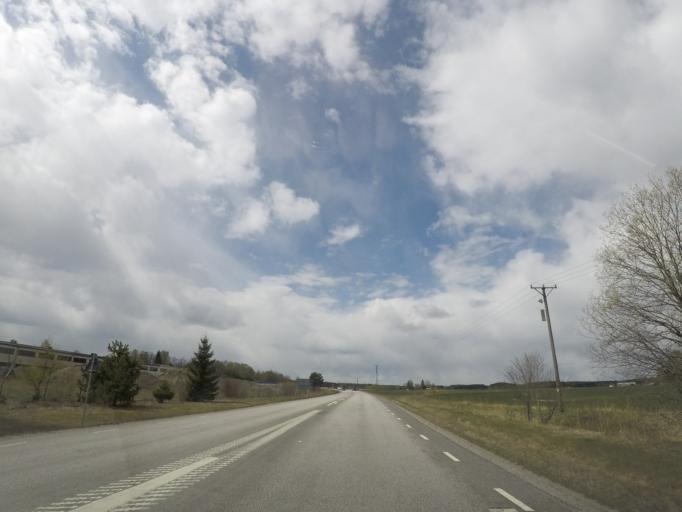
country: SE
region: Soedermanland
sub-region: Nykopings Kommun
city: Svalsta
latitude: 58.7432
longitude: 16.9136
